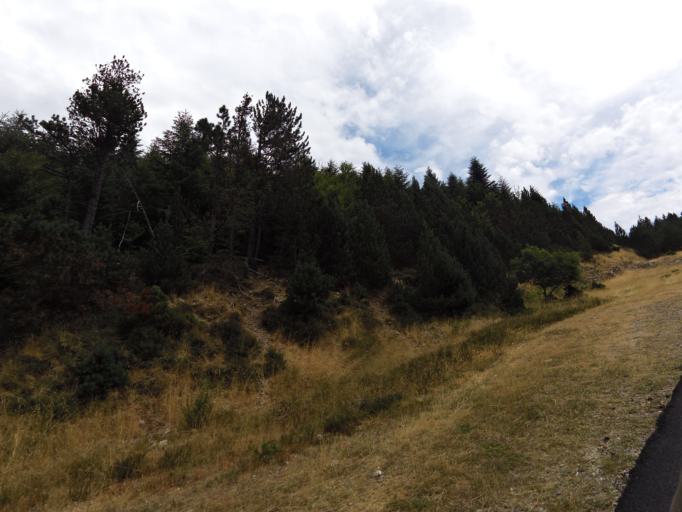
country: FR
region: Languedoc-Roussillon
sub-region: Departement du Gard
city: Valleraugue
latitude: 44.0703
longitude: 3.5898
